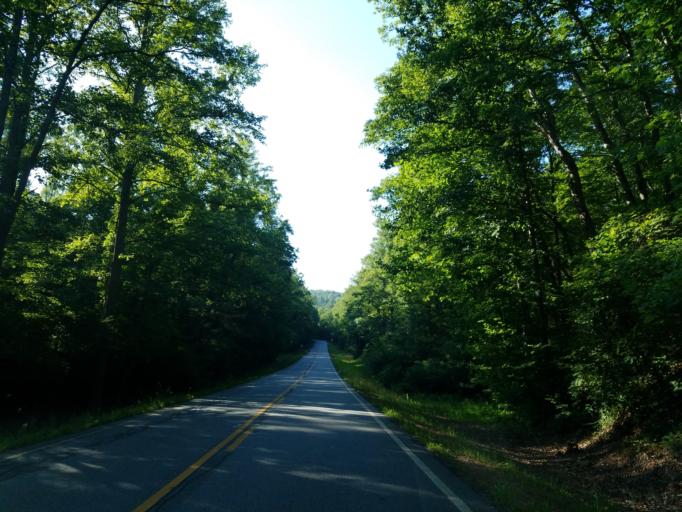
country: US
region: Georgia
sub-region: Fannin County
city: Blue Ridge
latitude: 34.7978
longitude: -84.1836
